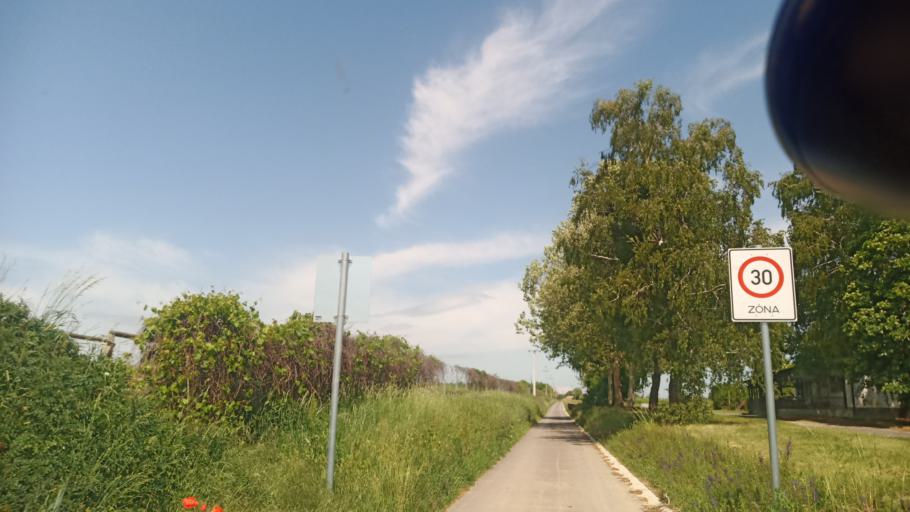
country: HU
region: Zala
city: Zalakomar
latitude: 46.6087
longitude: 17.1050
